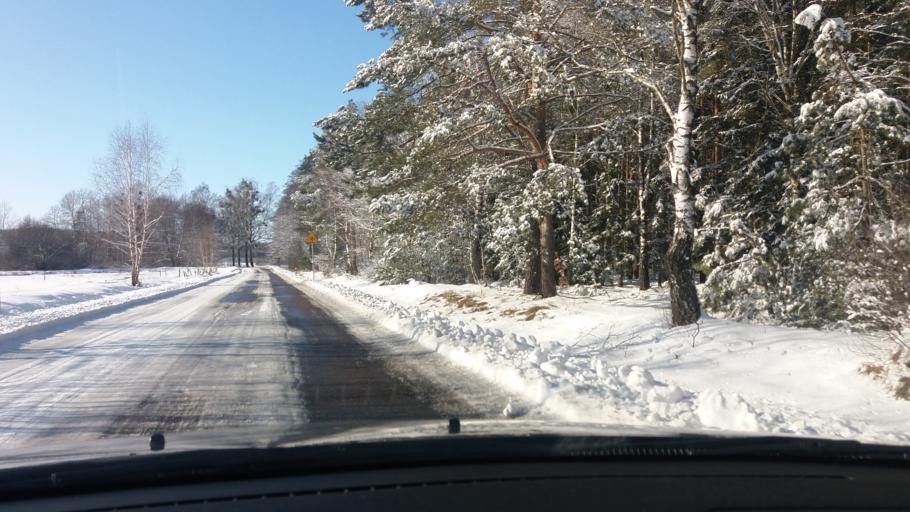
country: PL
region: Masovian Voivodeship
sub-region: Powiat mlawski
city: Dzierzgowo
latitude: 53.3339
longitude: 20.6304
